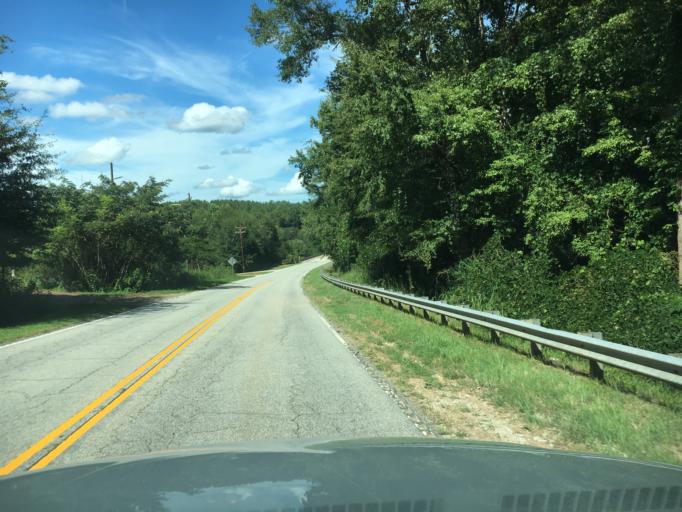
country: US
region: South Carolina
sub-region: Greenwood County
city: Ware Shoals
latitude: 34.4534
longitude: -82.1990
